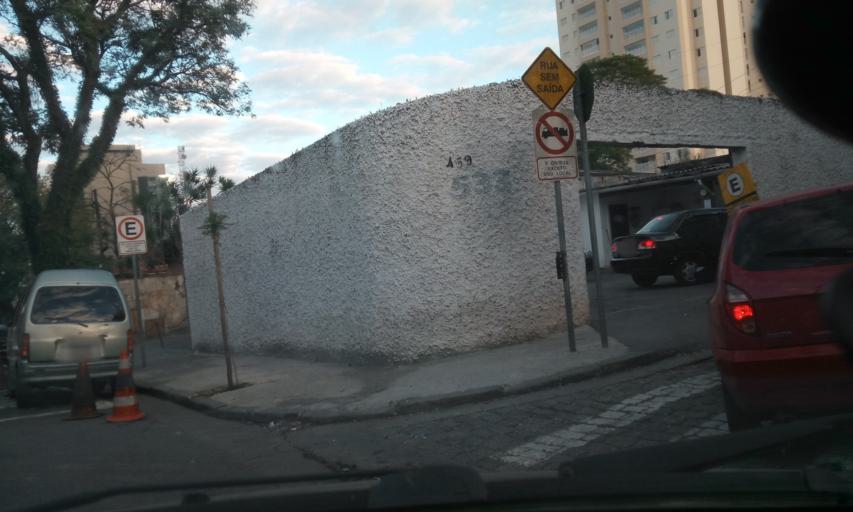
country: BR
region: Sao Paulo
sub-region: Sao Bernardo Do Campo
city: Sao Bernardo do Campo
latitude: -23.7138
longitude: -46.5447
